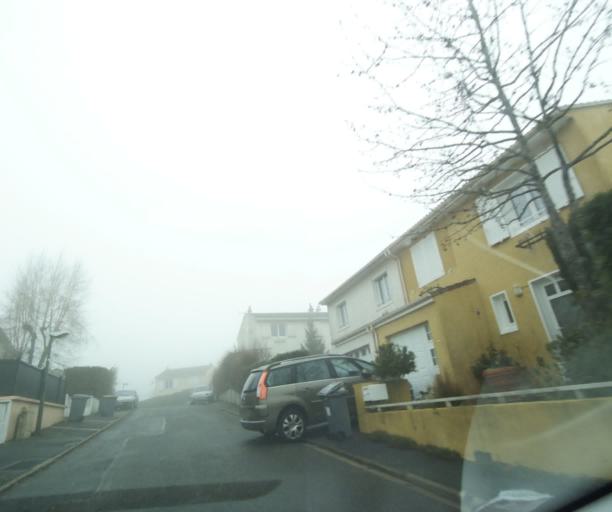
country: FR
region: Ile-de-France
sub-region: Departement de Seine-et-Marne
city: Dammartin-en-Goele
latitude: 49.0548
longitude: 2.6925
